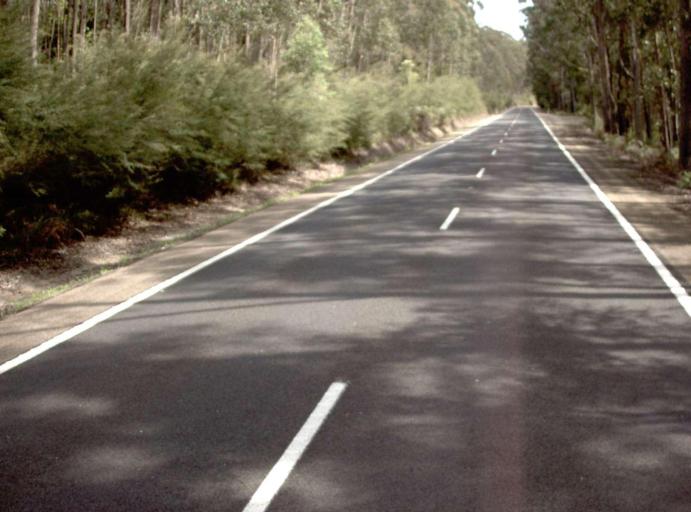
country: AU
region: New South Wales
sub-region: Bombala
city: Bombala
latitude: -37.5446
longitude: 149.3665
